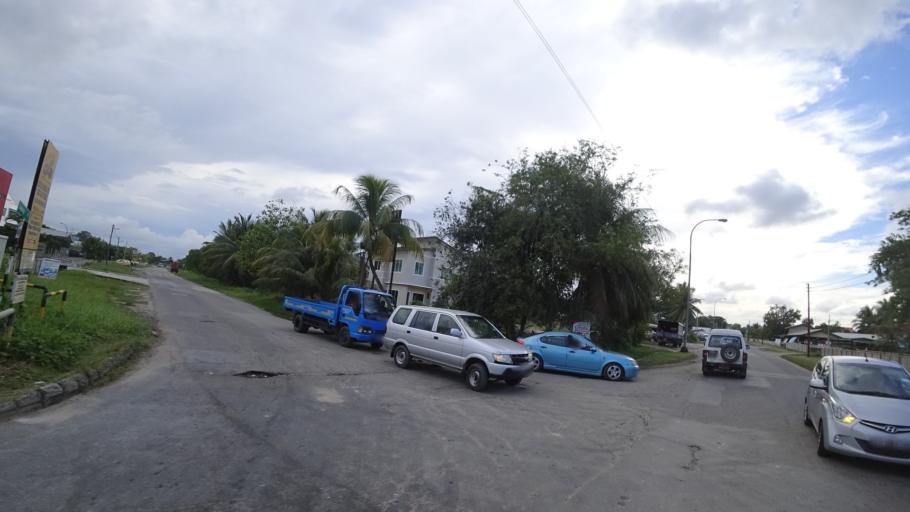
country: BN
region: Brunei and Muara
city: Bandar Seri Begawan
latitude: 4.8691
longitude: 114.8590
